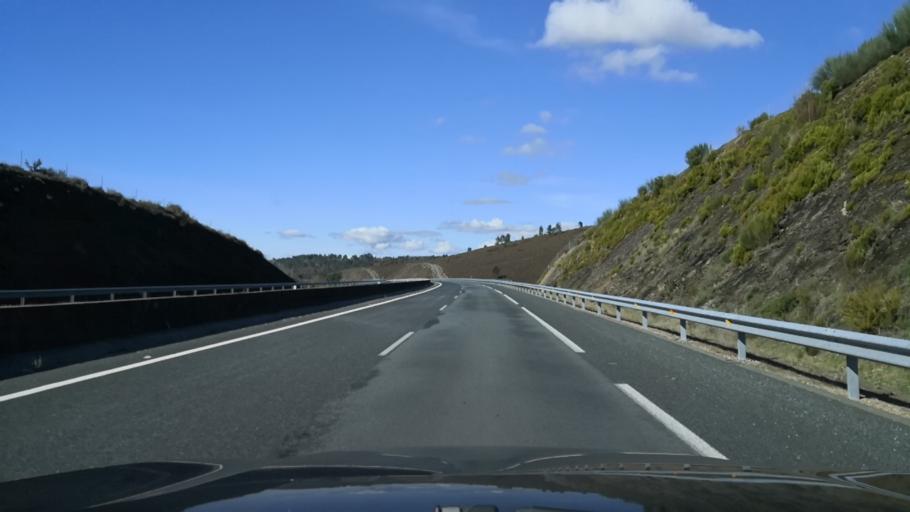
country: ES
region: Galicia
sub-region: Provincia de Pontevedra
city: Dozon
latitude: 42.5931
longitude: -8.0848
